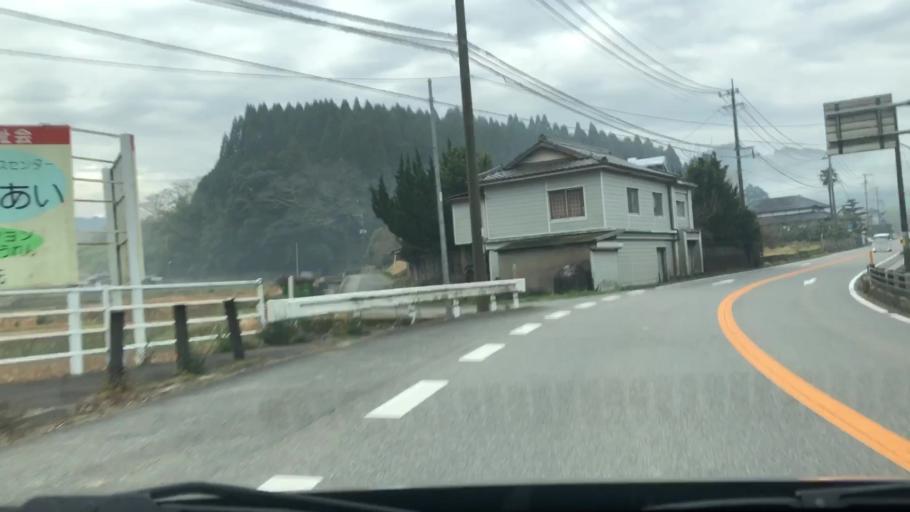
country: JP
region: Oita
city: Usuki
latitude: 33.0170
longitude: 131.7010
